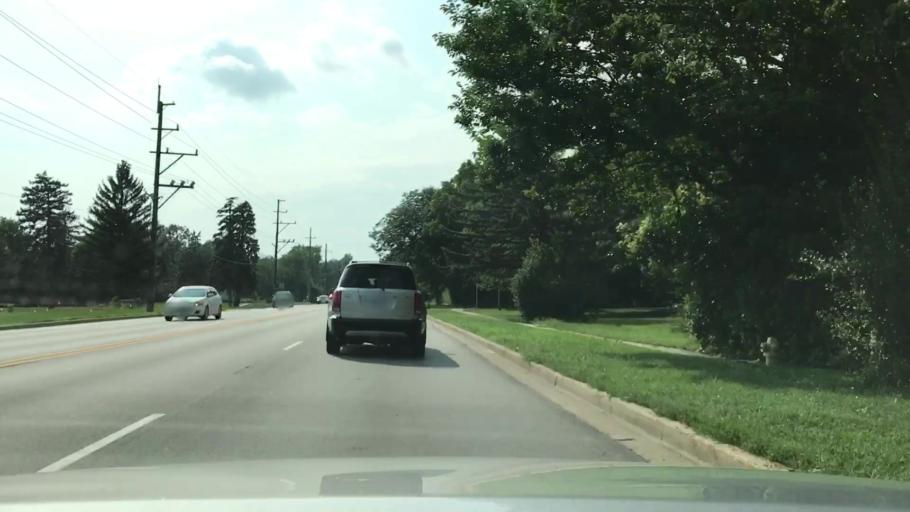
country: US
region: Illinois
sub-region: DuPage County
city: Westmont
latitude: 41.7733
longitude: -87.9963
